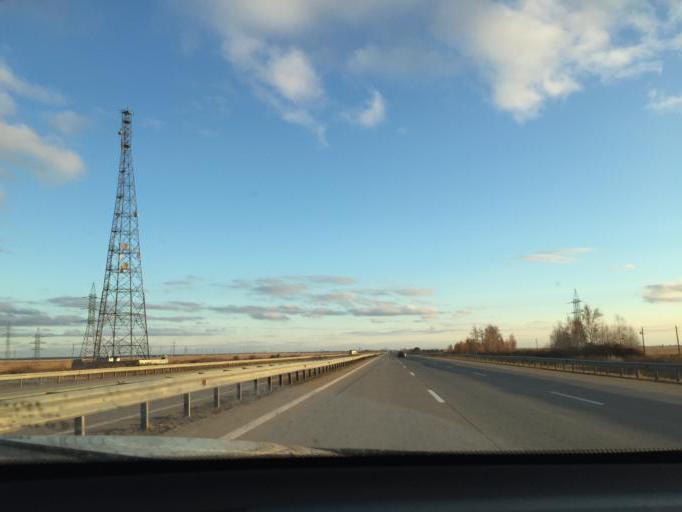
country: KZ
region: Astana Qalasy
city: Astana
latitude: 51.2989
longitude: 71.3562
